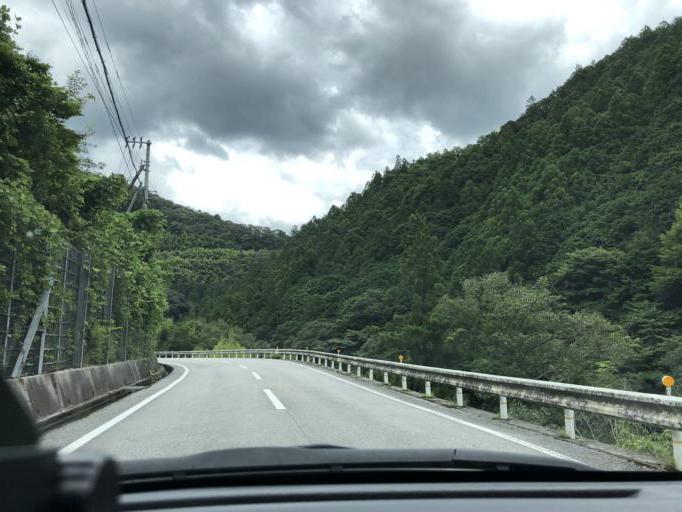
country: JP
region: Kochi
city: Kochi-shi
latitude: 33.6322
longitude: 133.5188
